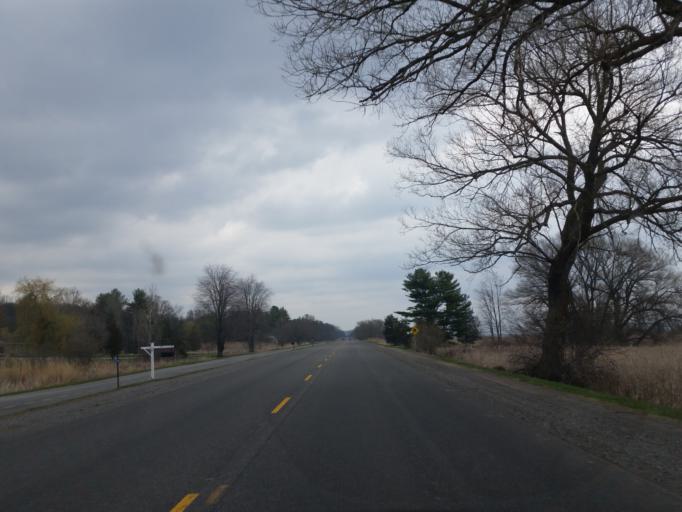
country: US
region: New York
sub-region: Jefferson County
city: Alexandria Bay
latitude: 44.4631
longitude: -75.8486
